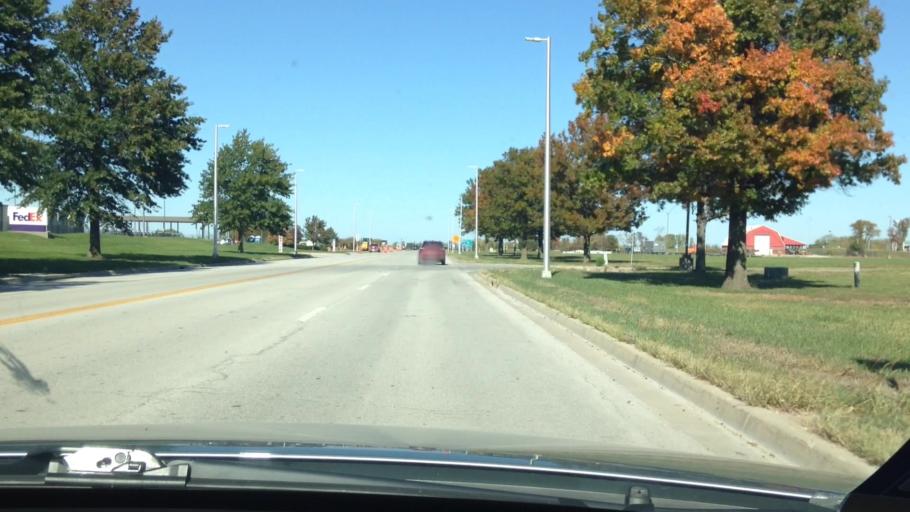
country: US
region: Missouri
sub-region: Platte County
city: Platte City
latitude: 39.3211
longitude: -94.7137
